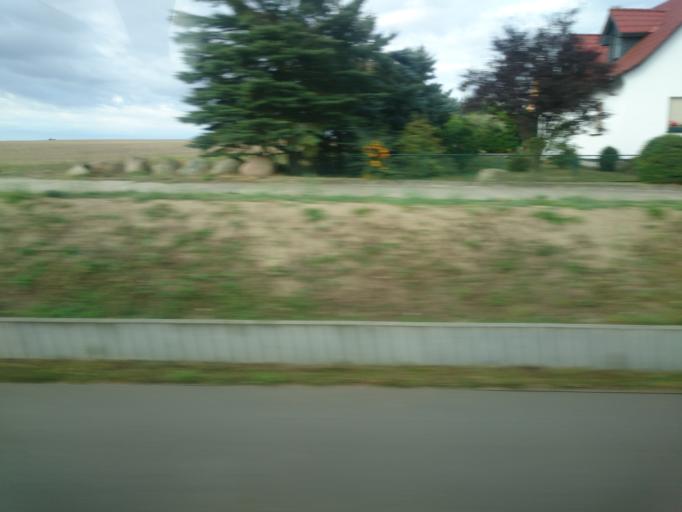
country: DE
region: Mecklenburg-Vorpommern
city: Pasewalk
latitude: 53.5415
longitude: 13.9705
